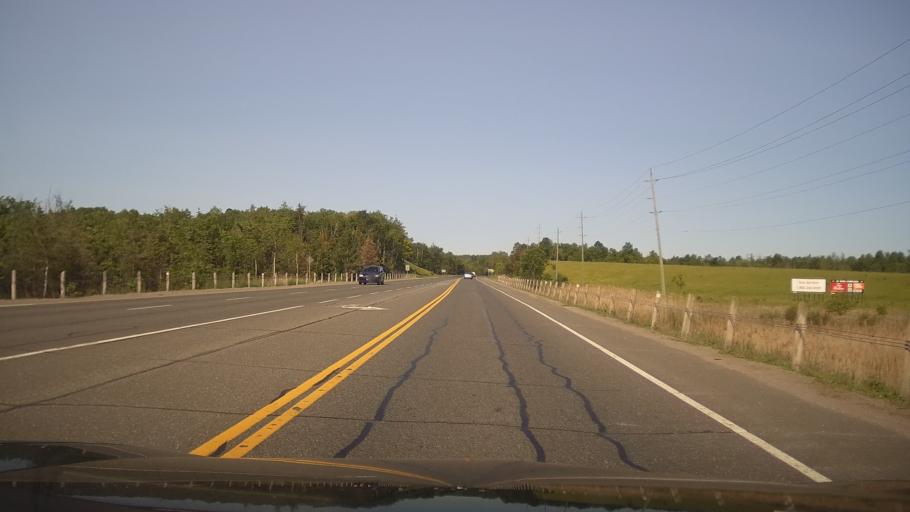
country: CA
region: Ontario
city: Peterborough
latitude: 44.3176
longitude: -78.1830
